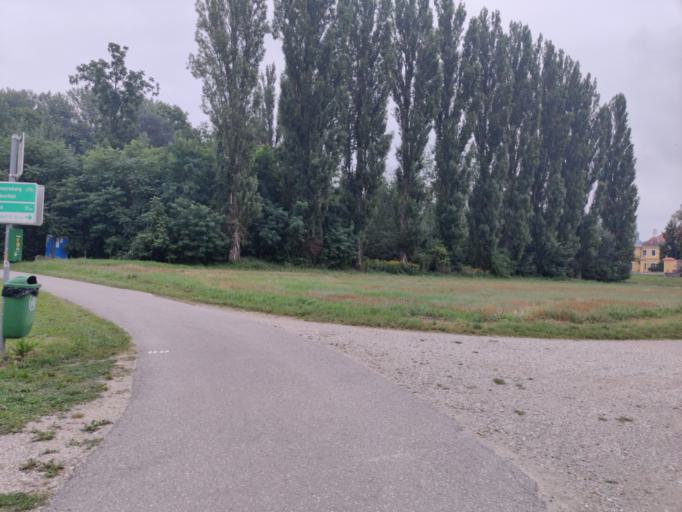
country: AT
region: Lower Austria
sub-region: Politischer Bezirk Tulln
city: Atzenbrugg
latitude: 48.3470
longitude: 15.9118
